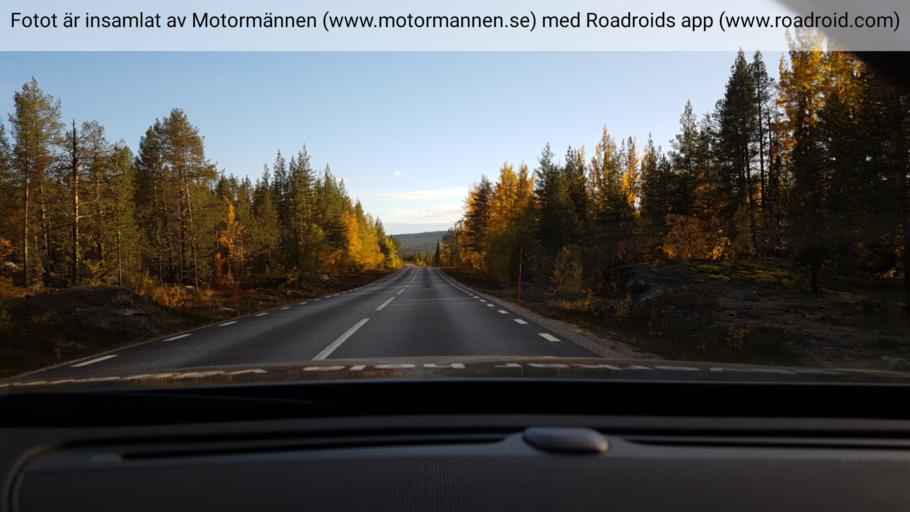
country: SE
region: Norrbotten
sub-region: Jokkmokks Kommun
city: Jokkmokk
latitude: 66.8754
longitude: 19.8220
